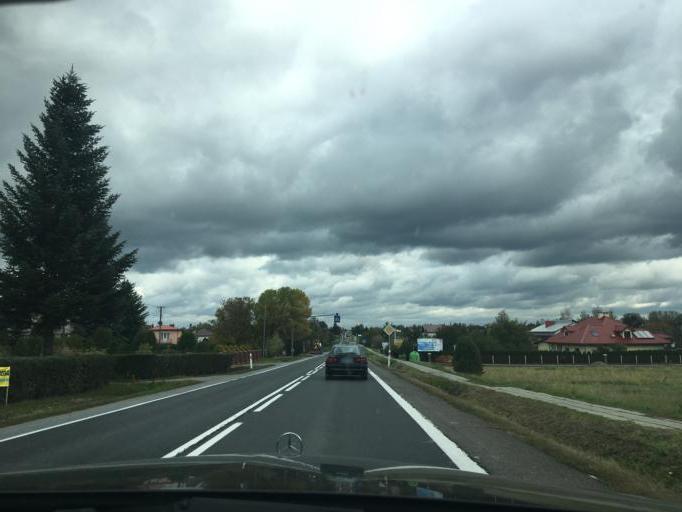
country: PL
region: Subcarpathian Voivodeship
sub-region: Powiat krosnienski
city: Miejsce Piastowe
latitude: 49.6197
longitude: 21.7599
